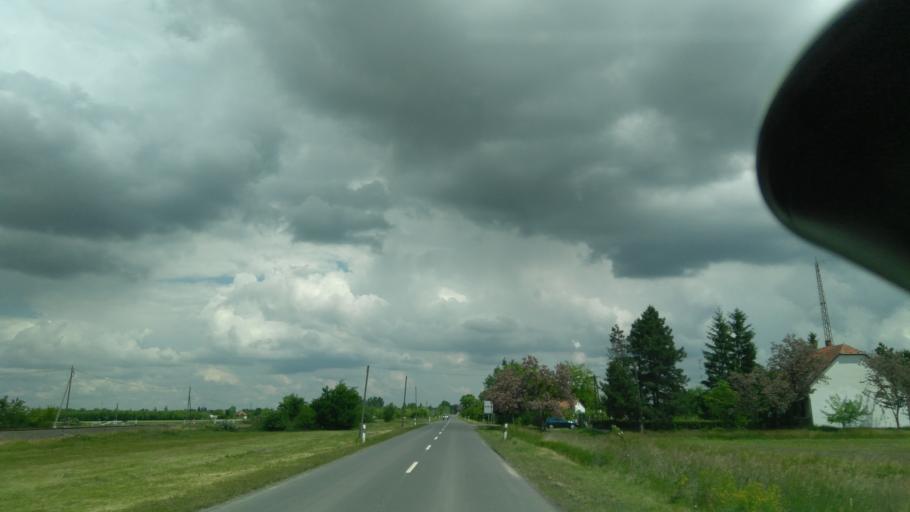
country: HU
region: Bekes
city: Devavanya
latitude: 47.0217
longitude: 20.9365
